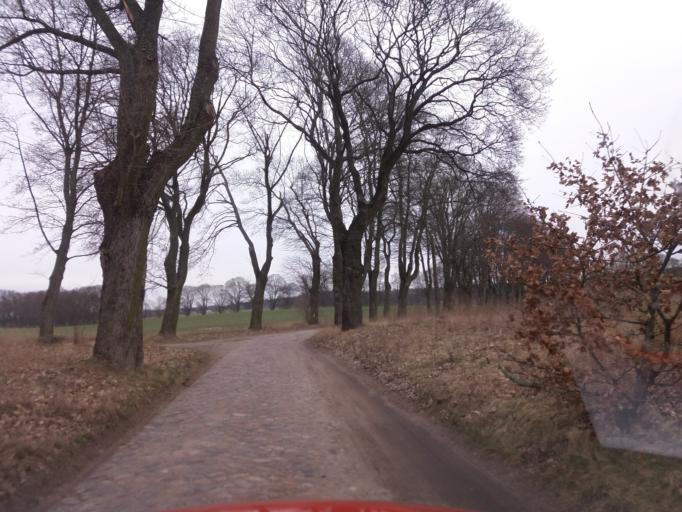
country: PL
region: West Pomeranian Voivodeship
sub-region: Powiat choszczenski
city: Recz
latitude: 53.1619
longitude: 15.6119
